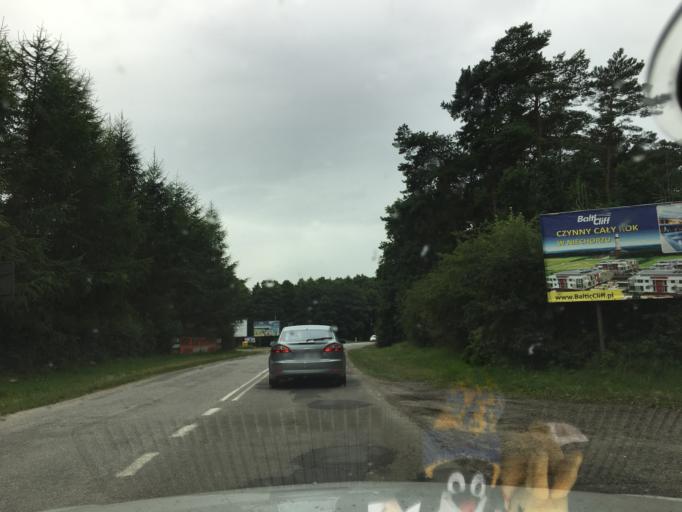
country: PL
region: West Pomeranian Voivodeship
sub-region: Powiat gryficki
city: Pobierowo
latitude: 54.0490
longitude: 14.9308
